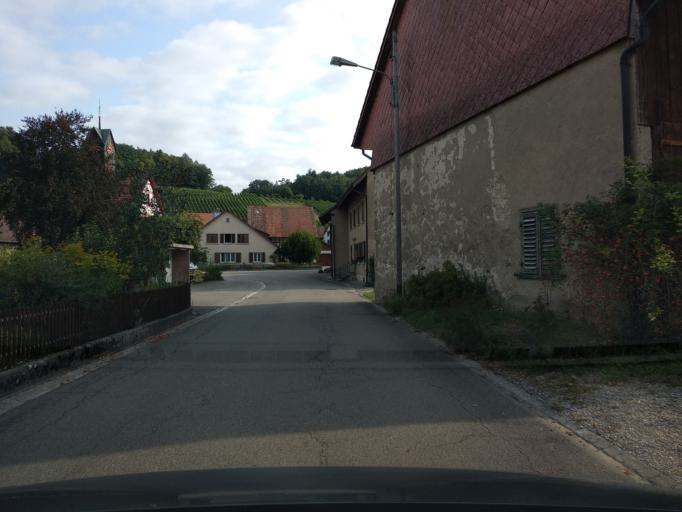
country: CH
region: Zurich
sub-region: Bezirk Andelfingen
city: Marthalen
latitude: 47.6399
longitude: 8.6730
